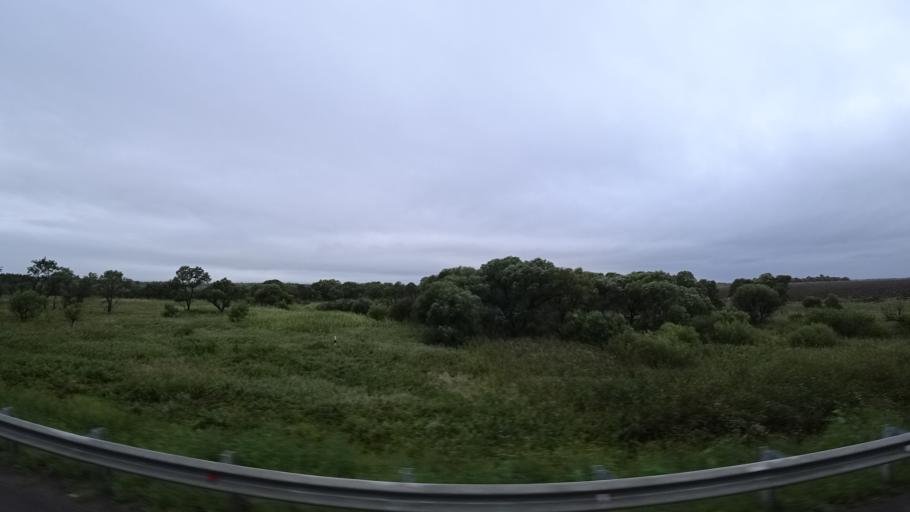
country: RU
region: Primorskiy
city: Chernigovka
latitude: 44.2932
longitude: 132.5131
